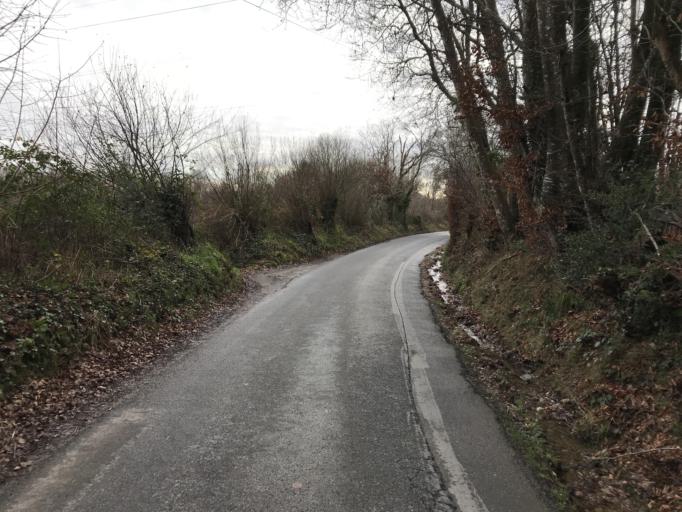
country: FR
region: Brittany
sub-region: Departement du Finistere
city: Plougastel-Daoulas
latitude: 48.3789
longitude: -4.3470
